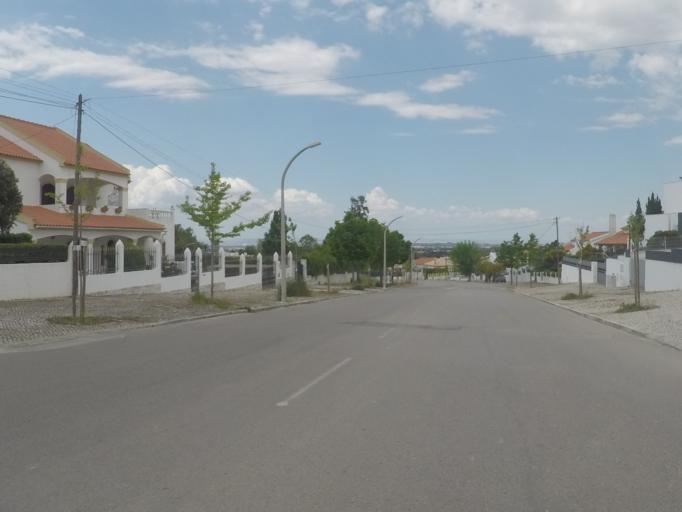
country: PT
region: Setubal
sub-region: Palmela
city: Quinta do Anjo
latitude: 38.5170
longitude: -9.0087
